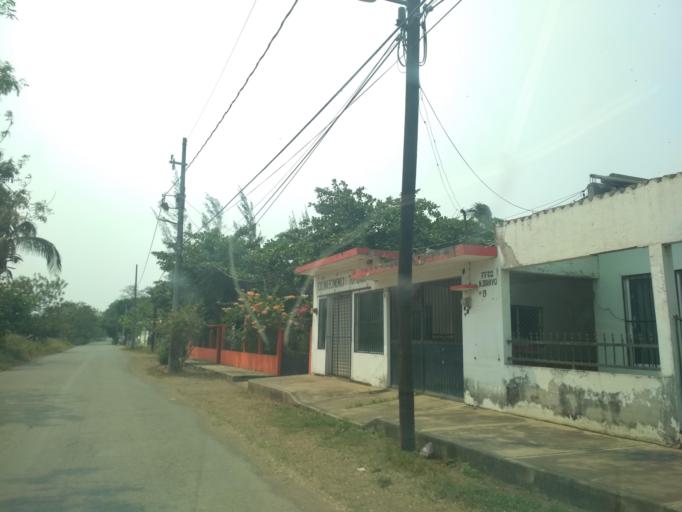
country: MX
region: Veracruz
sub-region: Veracruz
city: Delfino Victoria (Santa Fe)
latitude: 19.2045
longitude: -96.2698
